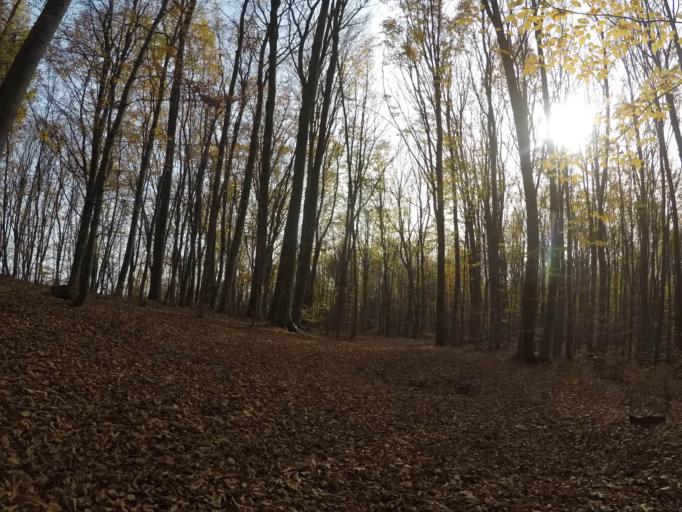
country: SK
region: Presovsky
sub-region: Okres Presov
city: Presov
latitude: 48.9560
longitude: 21.1858
